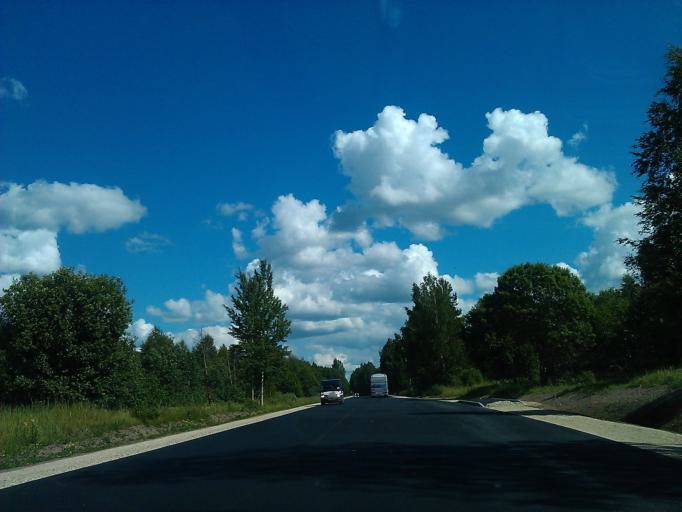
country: LV
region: Vilanu
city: Vilani
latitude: 56.5504
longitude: 27.0984
